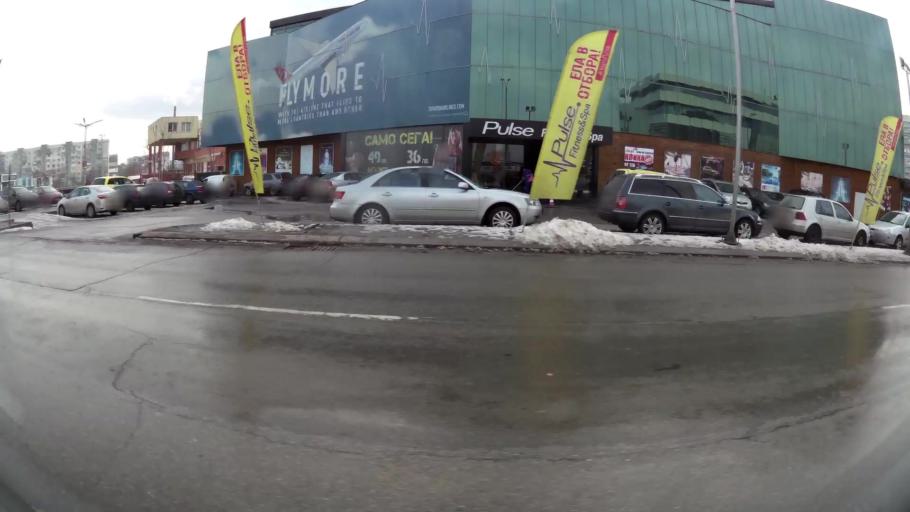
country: BG
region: Sofia-Capital
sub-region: Stolichna Obshtina
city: Sofia
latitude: 42.7097
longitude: 23.3658
